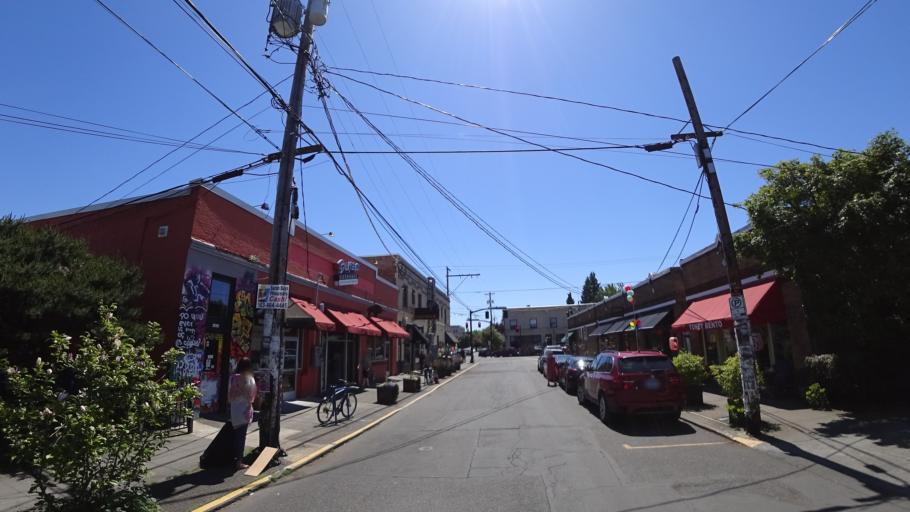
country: US
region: Oregon
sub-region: Multnomah County
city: Portland
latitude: 45.5126
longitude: -122.6259
